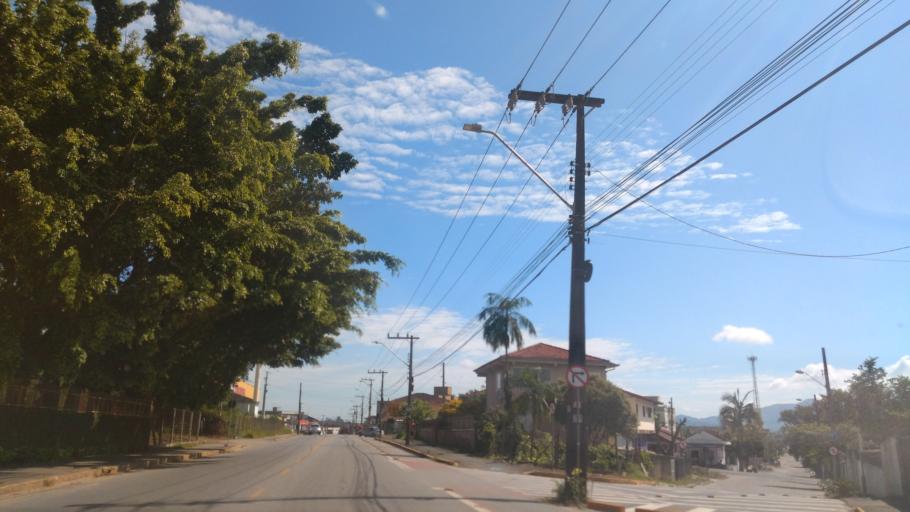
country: BR
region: Santa Catarina
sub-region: Joinville
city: Joinville
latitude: -26.2393
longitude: -48.8185
